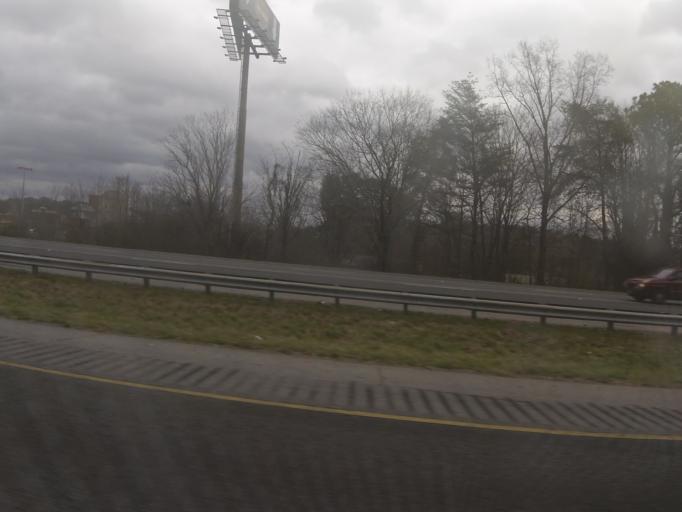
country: US
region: Georgia
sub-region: Whitfield County
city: Dalton
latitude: 34.7562
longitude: -85.0024
